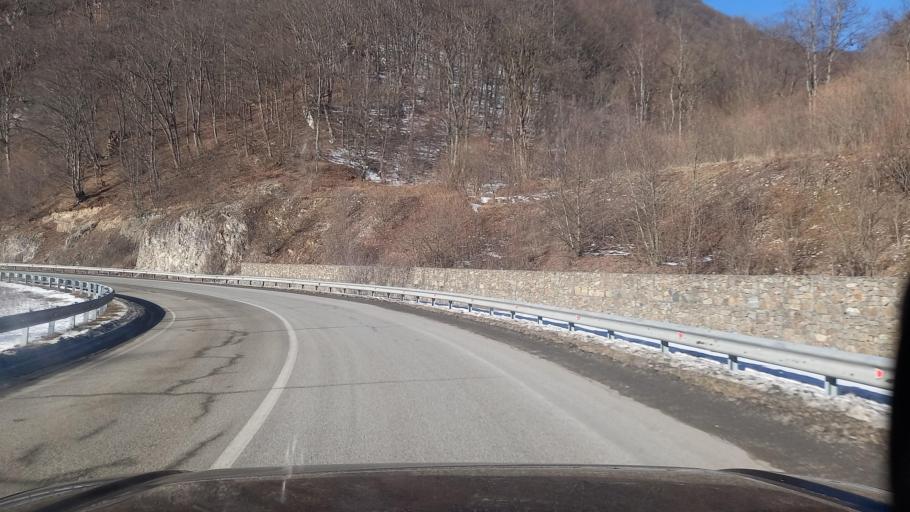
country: RU
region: North Ossetia
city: Gizel'
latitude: 42.9324
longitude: 44.5469
